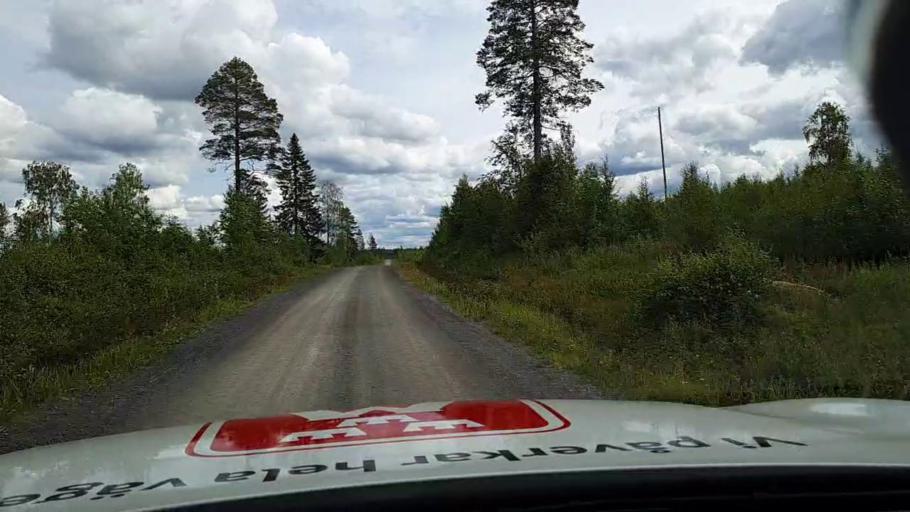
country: SE
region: Jaemtland
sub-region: OEstersunds Kommun
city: Lit
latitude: 63.2970
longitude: 15.3296
